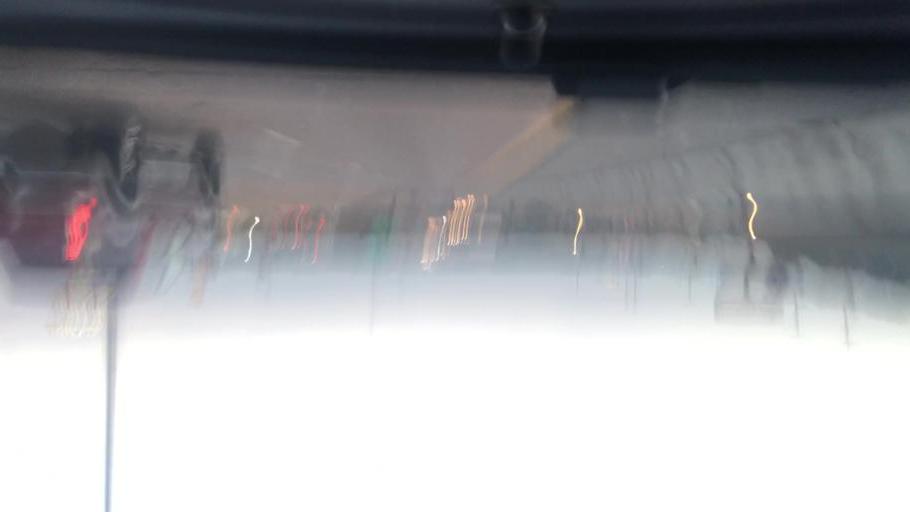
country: US
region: Texas
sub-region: Dallas County
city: DeSoto
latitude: 32.6647
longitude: -96.8230
